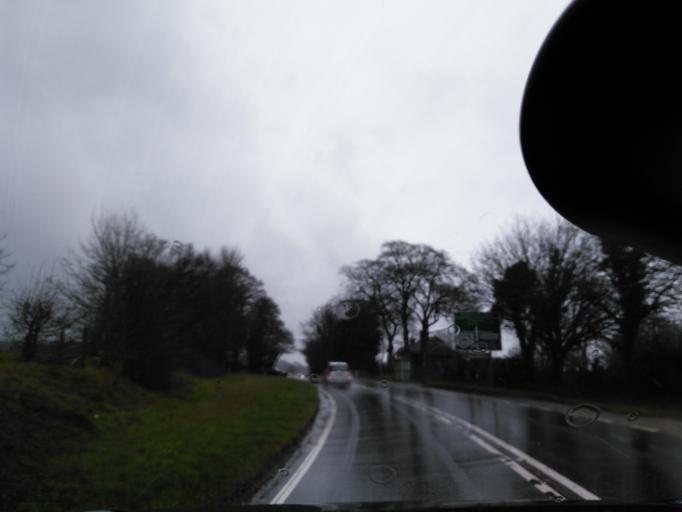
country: GB
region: England
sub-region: Somerset
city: Evercreech
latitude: 51.1884
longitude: -2.4823
